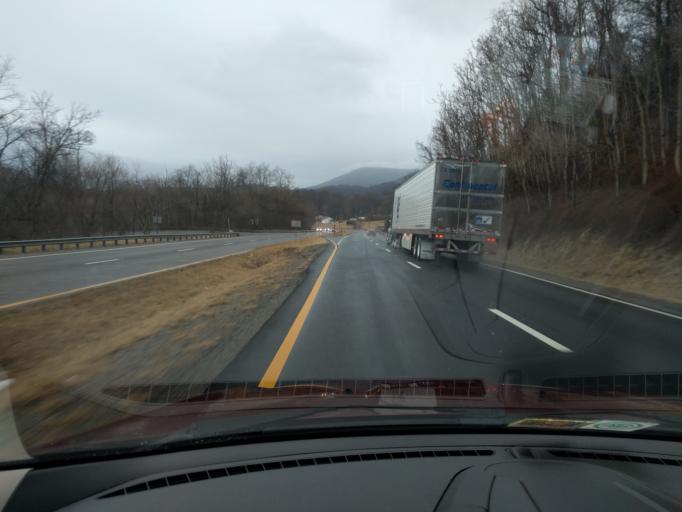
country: US
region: Virginia
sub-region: Giles County
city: Pembroke
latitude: 37.3178
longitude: -80.5886
